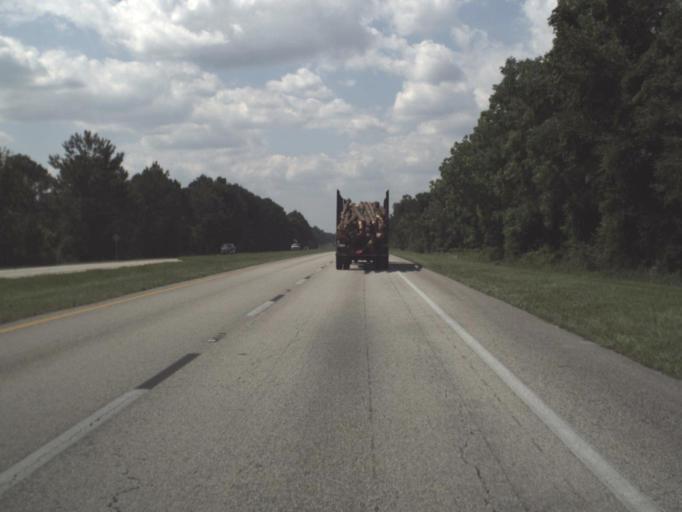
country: US
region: Florida
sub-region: Alachua County
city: Hawthorne
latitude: 29.6776
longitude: -82.1225
